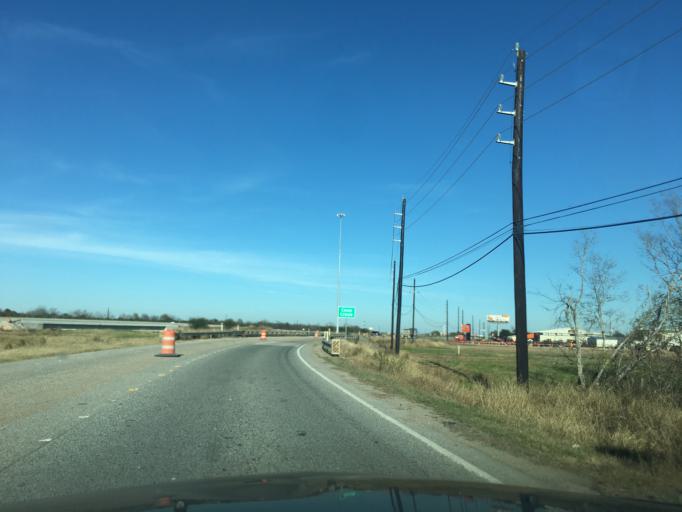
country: US
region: Texas
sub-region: Fort Bend County
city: Rosenberg
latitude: 29.5239
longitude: -95.8716
